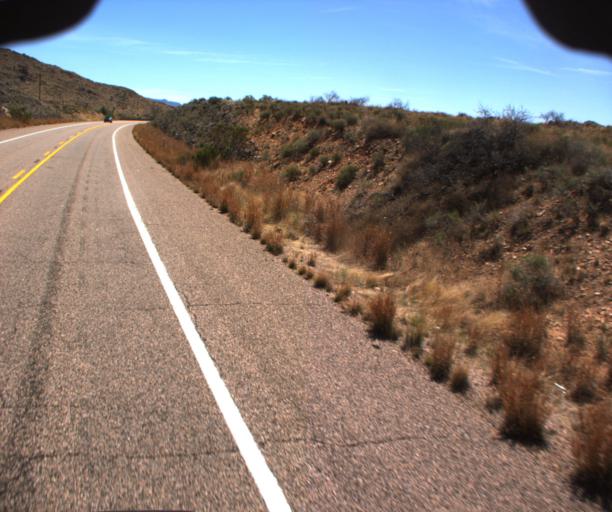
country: US
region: Arizona
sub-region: Mohave County
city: New Kingman-Butler
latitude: 35.3872
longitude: -113.7364
